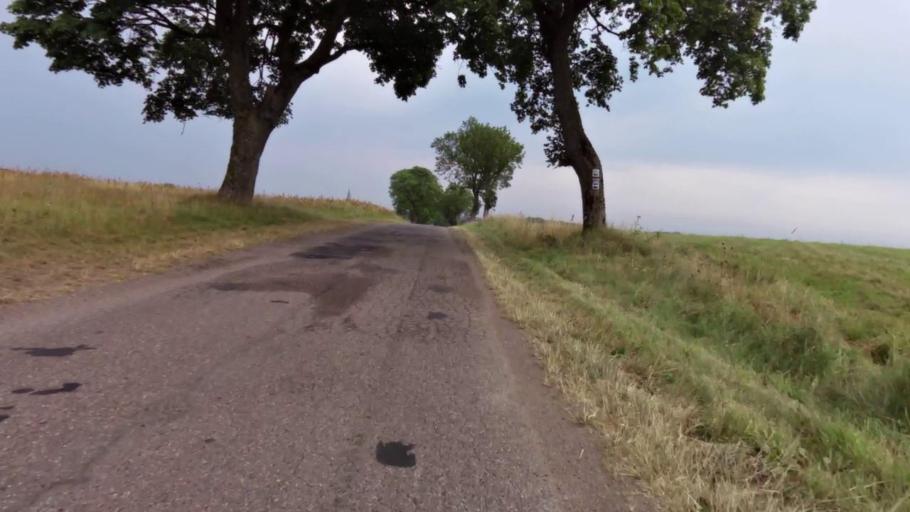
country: PL
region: West Pomeranian Voivodeship
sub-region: Powiat drawski
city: Drawsko Pomorskie
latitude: 53.5314
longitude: 15.7890
